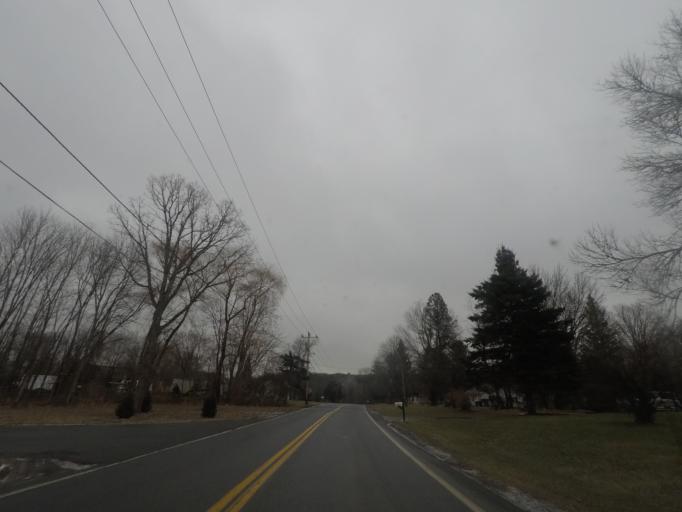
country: US
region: New York
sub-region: Saratoga County
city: Country Knolls
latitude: 42.9160
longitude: -73.7598
